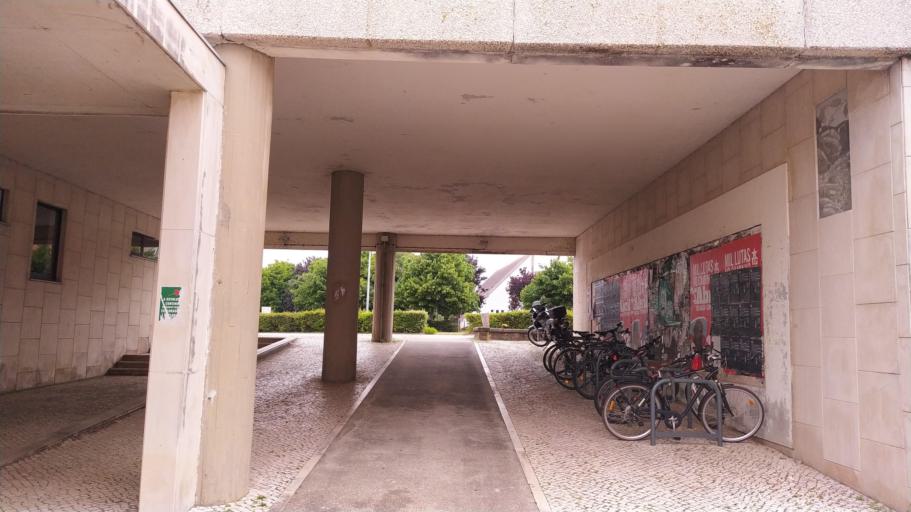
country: PT
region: Aveiro
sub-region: Aveiro
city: Aveiro
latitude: 40.6323
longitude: -8.6591
